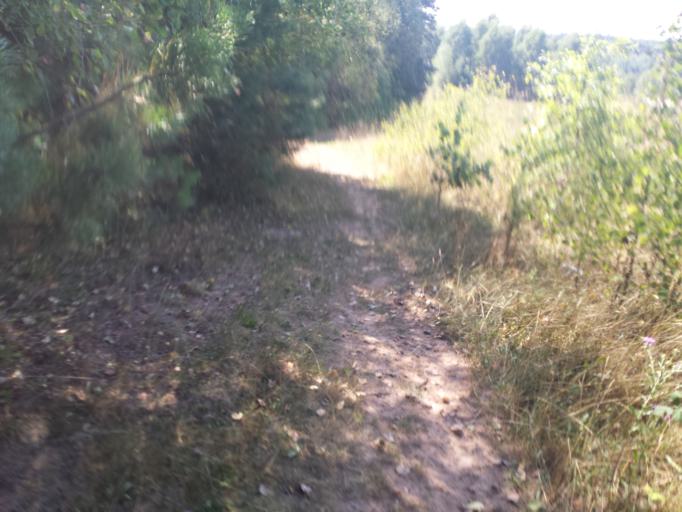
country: PL
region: Swietokrzyskie
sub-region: Powiat kielecki
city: Daleszyce
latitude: 50.8025
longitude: 20.7696
